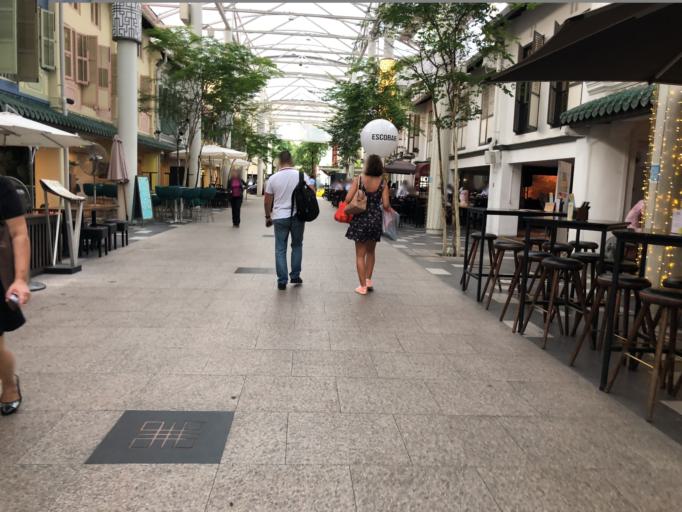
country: SG
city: Singapore
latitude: 1.2841
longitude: 103.8474
